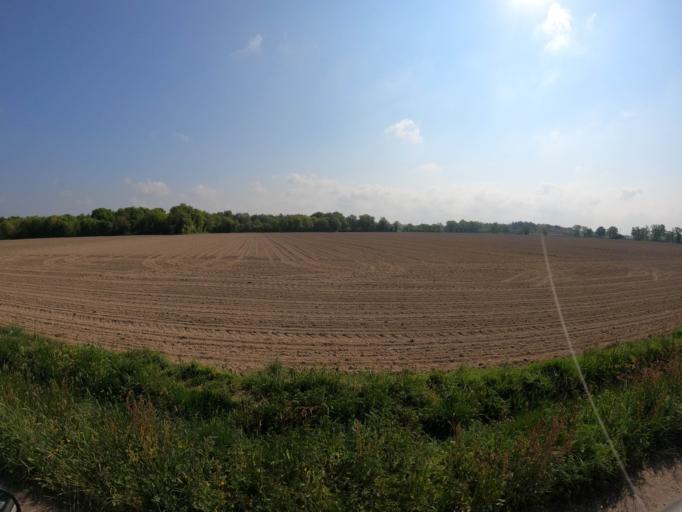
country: FR
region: Pays de la Loire
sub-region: Departement de la Vendee
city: Treize-Septiers
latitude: 47.0045
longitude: -1.2497
